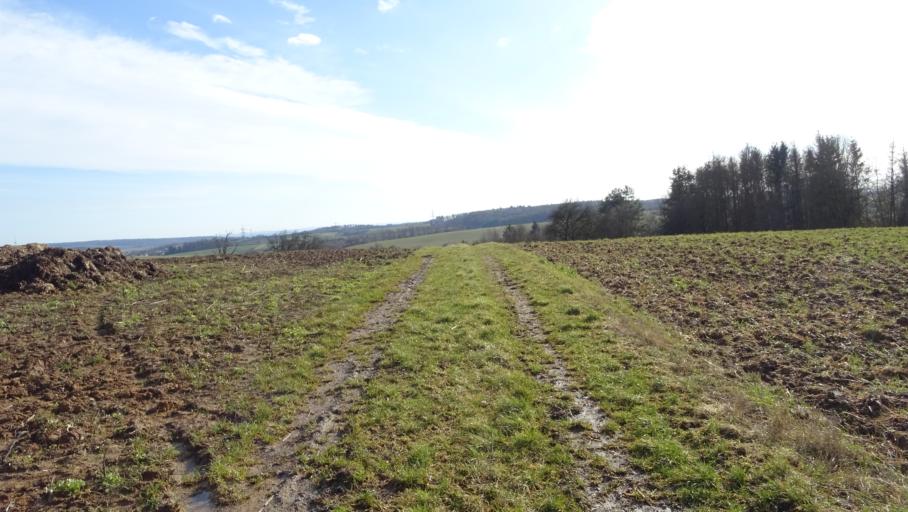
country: DE
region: Baden-Wuerttemberg
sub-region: Karlsruhe Region
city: Mosbach
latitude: 49.3677
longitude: 9.1912
